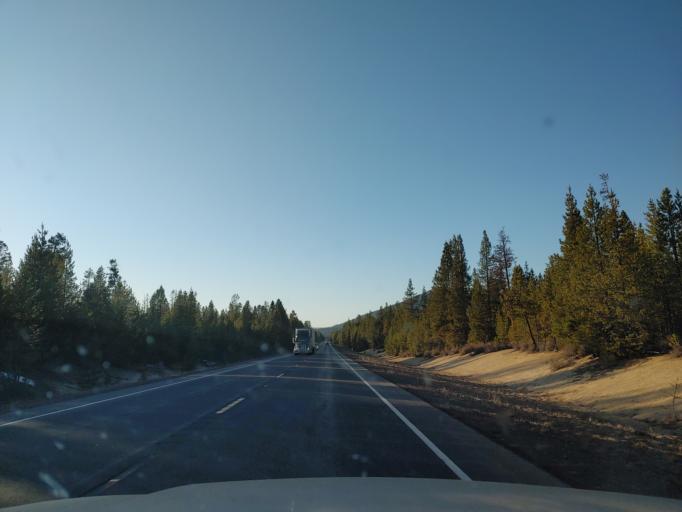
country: US
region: Oregon
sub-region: Deschutes County
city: La Pine
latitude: 43.4024
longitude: -121.8230
